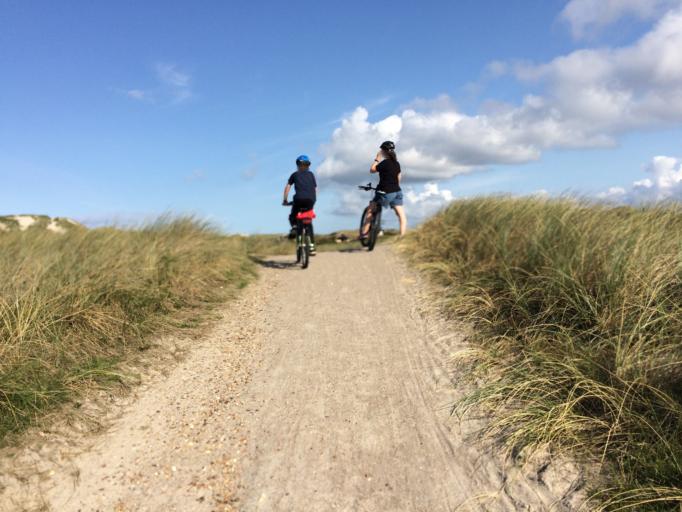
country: DK
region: Central Jutland
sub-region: Ringkobing-Skjern Kommune
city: Hvide Sande
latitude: 55.9221
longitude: 8.1528
